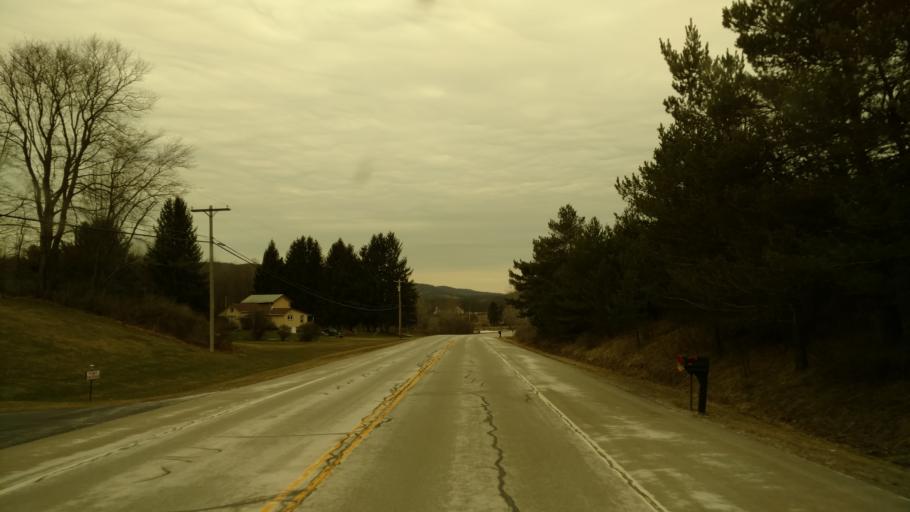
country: US
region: New York
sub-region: Allegany County
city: Wellsville
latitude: 42.0410
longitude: -77.9148
